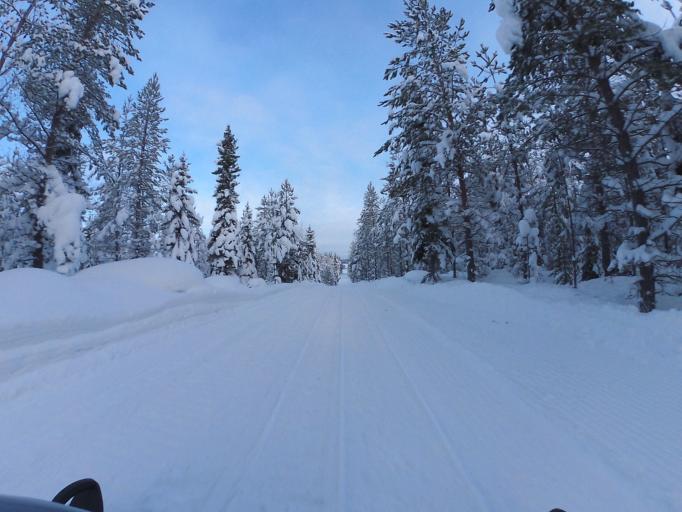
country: FI
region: Lapland
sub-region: Rovaniemi
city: Rovaniemi
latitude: 66.5329
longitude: 26.0390
